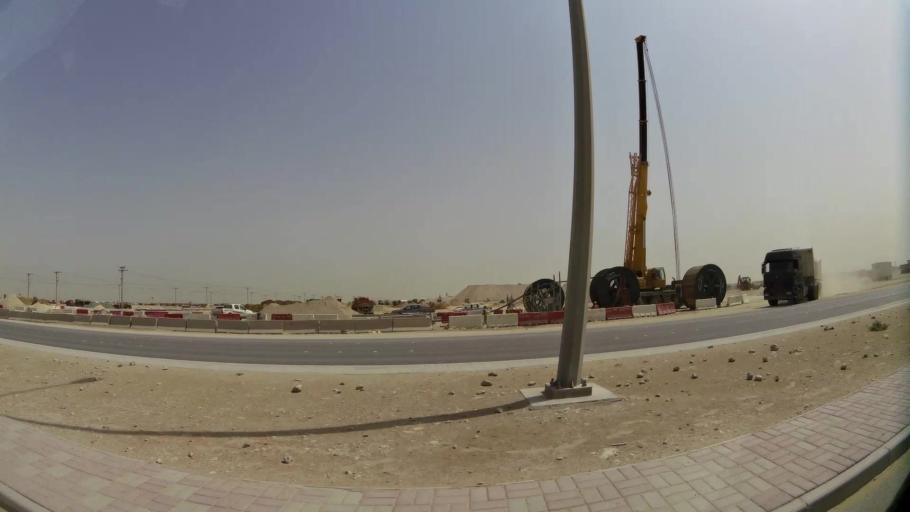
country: QA
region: Baladiyat ar Rayyan
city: Ar Rayyan
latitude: 25.1746
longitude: 51.3994
